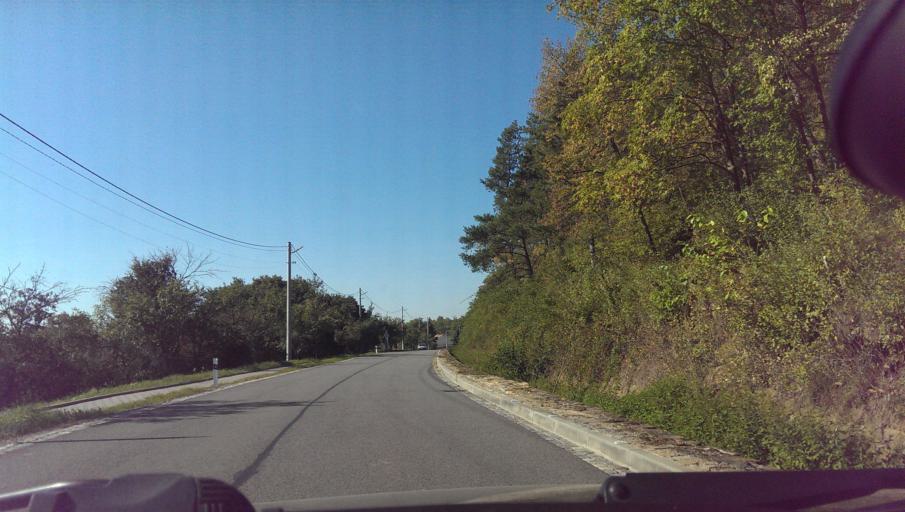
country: CZ
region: Zlin
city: Popovice
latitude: 49.0469
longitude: 17.5269
